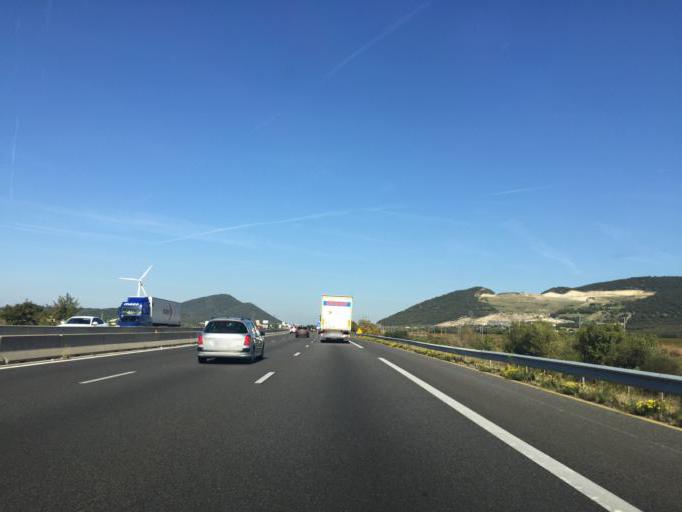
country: FR
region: Rhone-Alpes
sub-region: Departement de la Drome
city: Donzere
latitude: 44.4419
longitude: 4.7520
